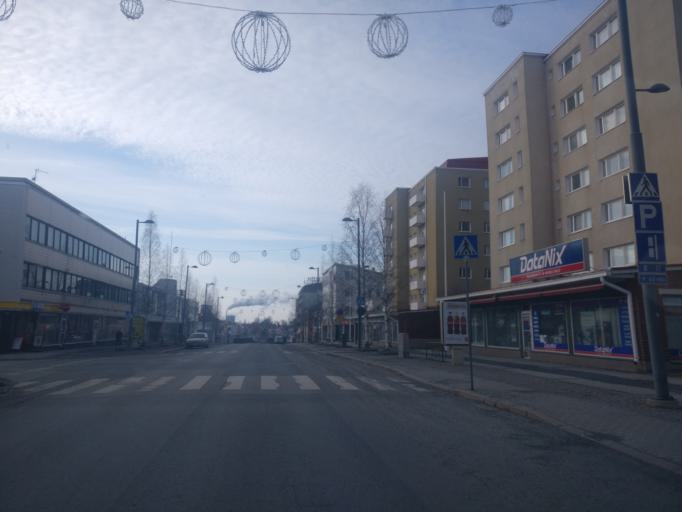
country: FI
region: Lapland
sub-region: Kemi-Tornio
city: Kemi
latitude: 65.7360
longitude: 24.5682
